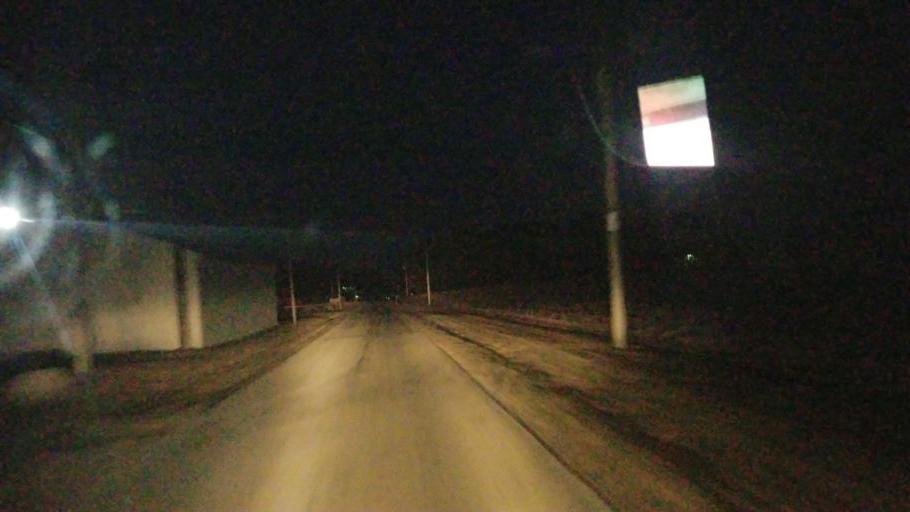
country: US
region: Ohio
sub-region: Defiance County
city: Hicksville
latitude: 41.3393
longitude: -84.7224
